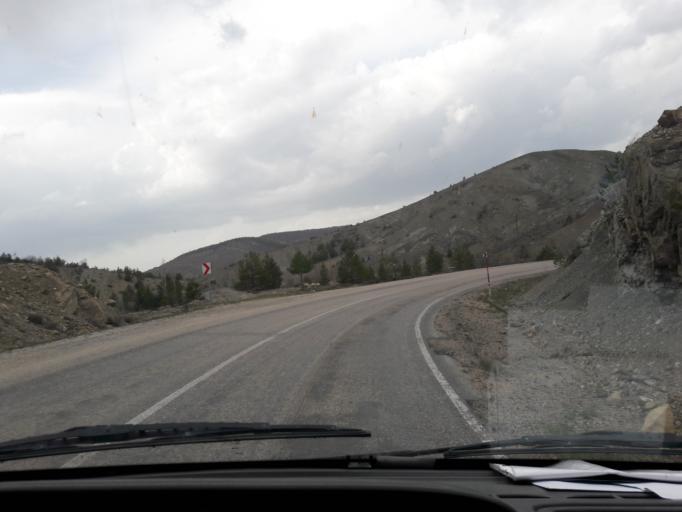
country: TR
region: Giresun
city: Alucra
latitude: 40.2775
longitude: 38.8222
